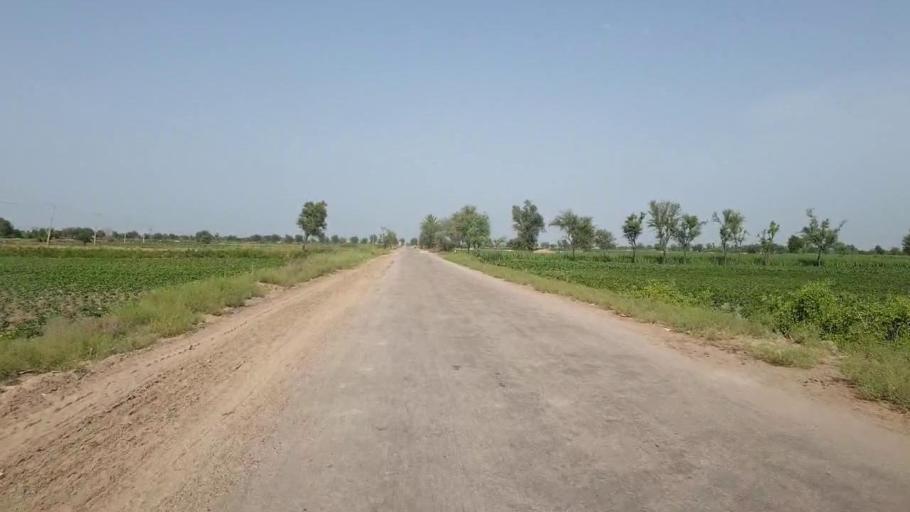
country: PK
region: Sindh
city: Sakrand
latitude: 26.2847
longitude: 68.2276
